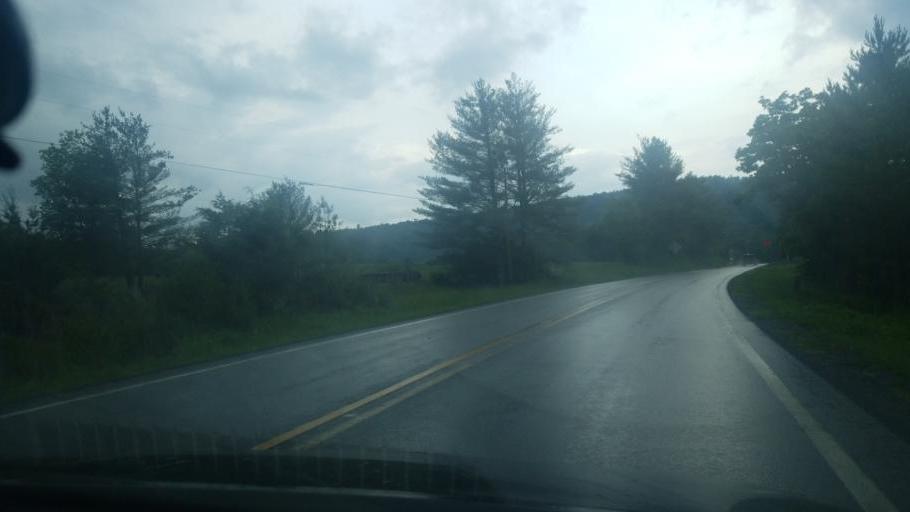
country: US
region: West Virginia
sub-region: Pendleton County
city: Franklin
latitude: 38.6705
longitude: -79.2716
